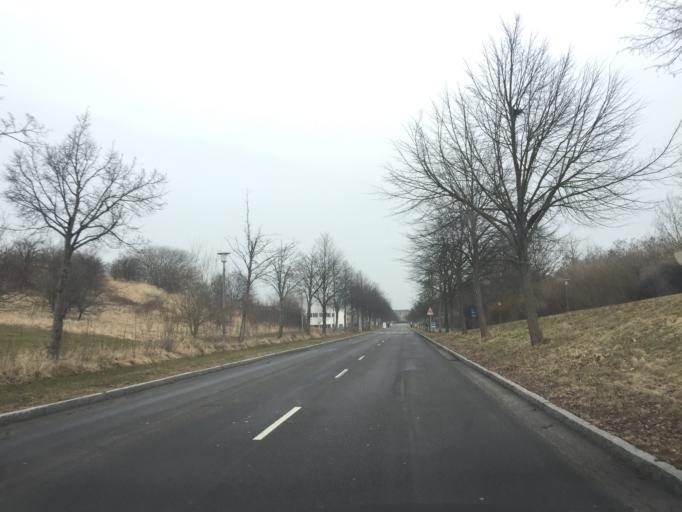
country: DK
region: Capital Region
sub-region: Hoje-Taastrup Kommune
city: Taastrup
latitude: 55.6484
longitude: 12.2592
